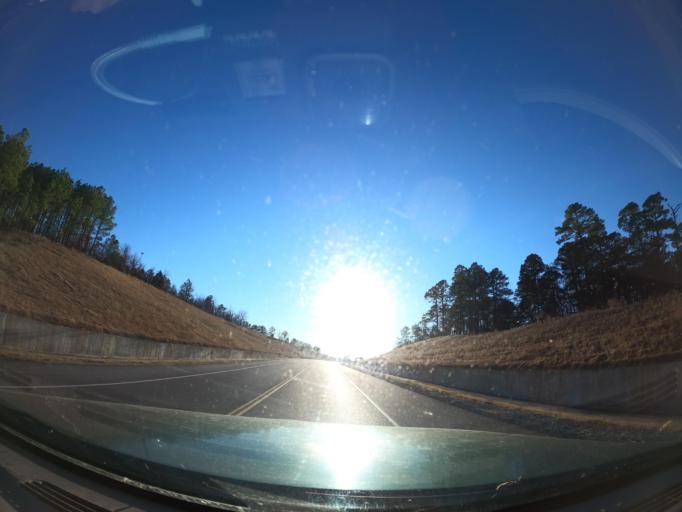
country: US
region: Oklahoma
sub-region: Pittsburg County
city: Hartshorne
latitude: 34.8895
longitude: -95.4586
